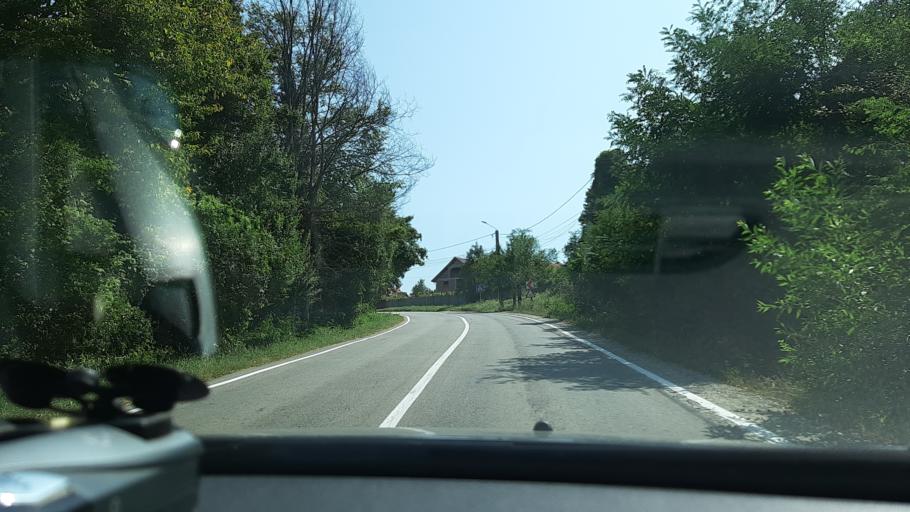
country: RO
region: Gorj
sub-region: Comuna Targu Carbunesti
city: Targu Carbunesti
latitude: 44.9428
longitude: 23.5329
